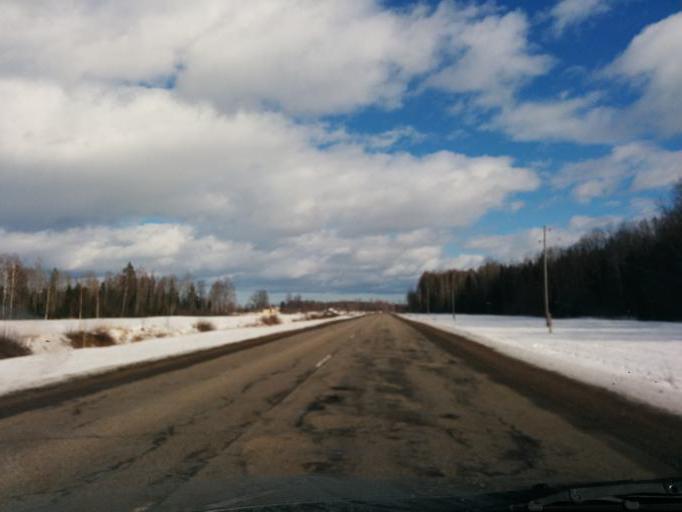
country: LV
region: Gulbenes Rajons
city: Gulbene
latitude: 57.1823
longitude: 26.8416
